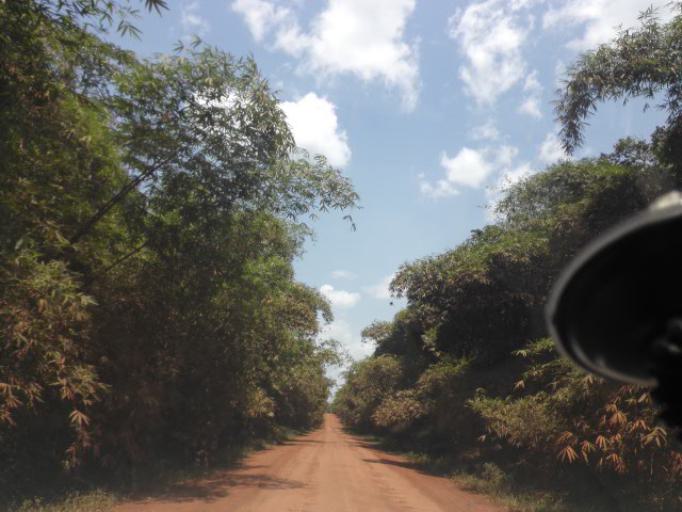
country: CD
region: Eastern Province
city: Kisangani
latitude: 0.6282
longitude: 26.0664
